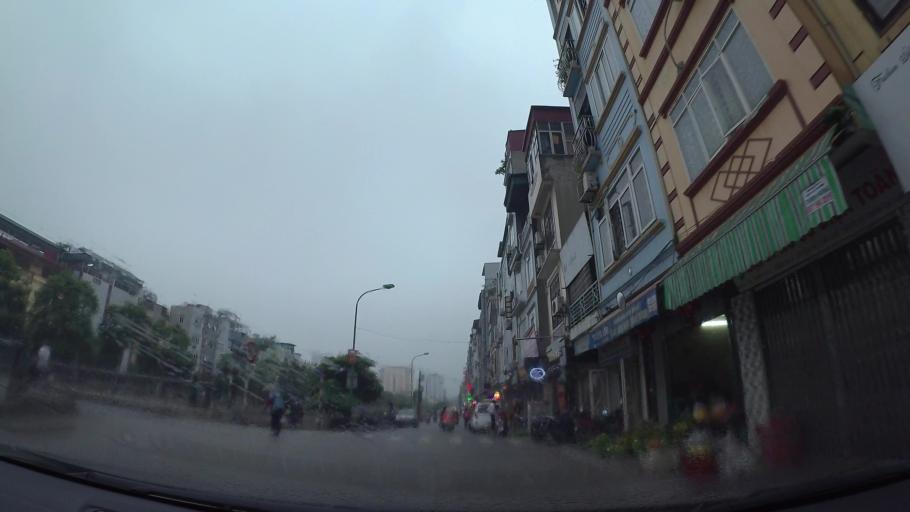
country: VN
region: Ha Noi
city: Hai BaTrung
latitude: 20.9929
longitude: 105.8365
